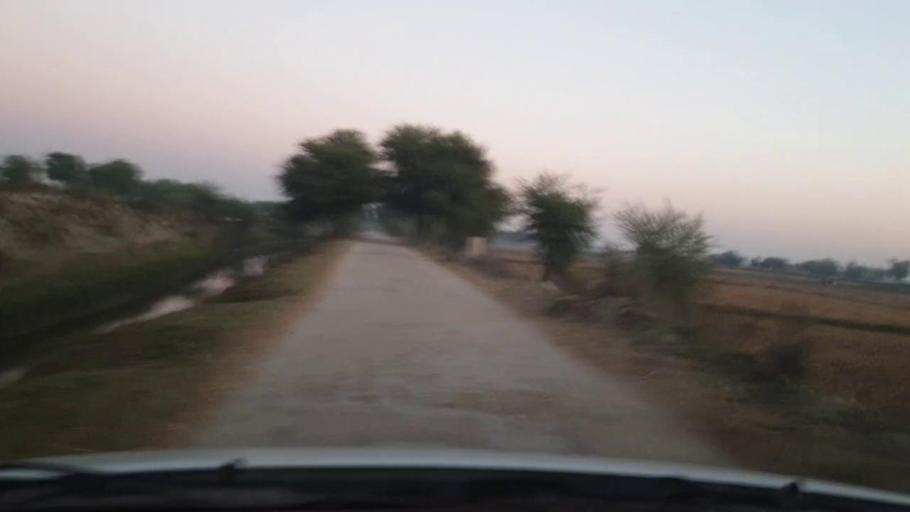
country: PK
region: Sindh
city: Khairpur Nathan Shah
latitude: 27.1495
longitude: 67.6953
